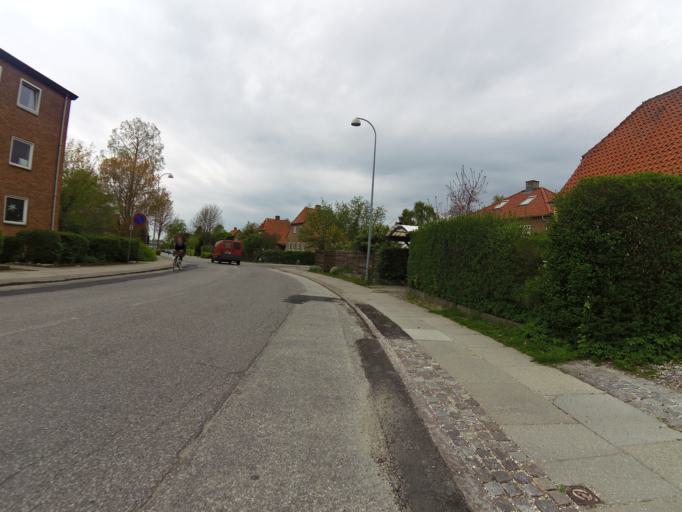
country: DK
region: Capital Region
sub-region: Gladsaxe Municipality
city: Buddinge
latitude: 55.7441
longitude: 12.4993
